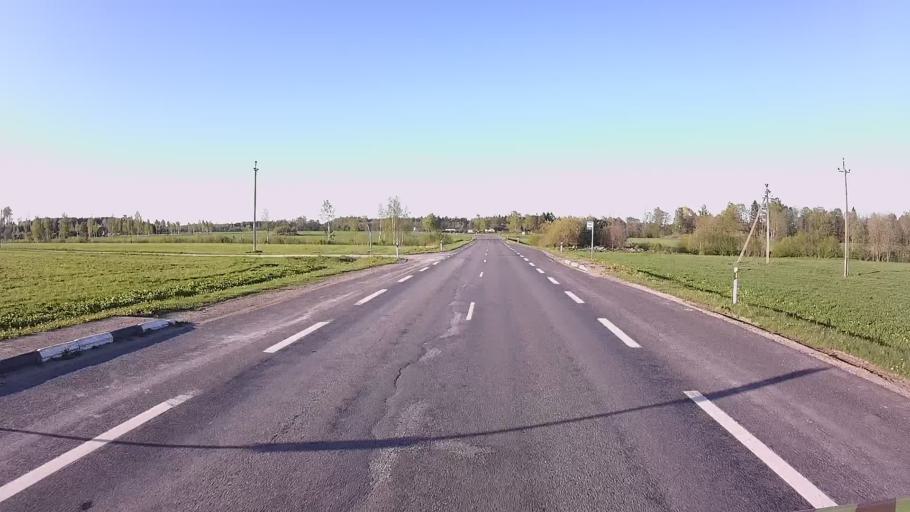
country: EE
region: Jogevamaa
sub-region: Poltsamaa linn
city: Poltsamaa
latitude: 58.4921
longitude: 25.8302
